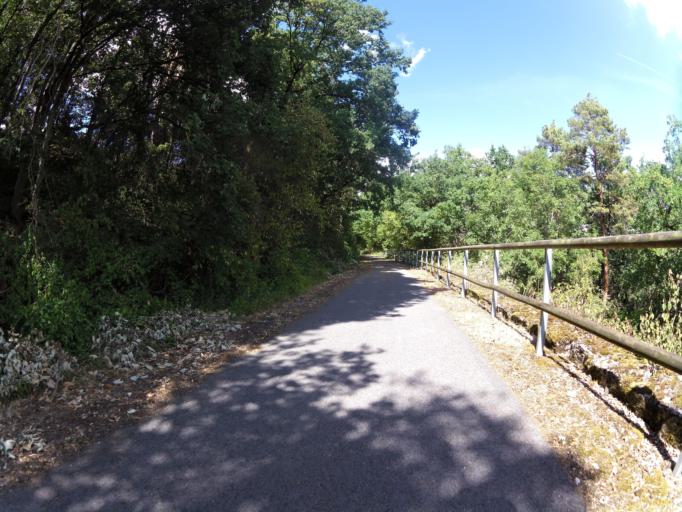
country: DE
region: Bavaria
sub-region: Regierungsbezirk Unterfranken
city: Bieberehren
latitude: 49.5245
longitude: 10.0319
